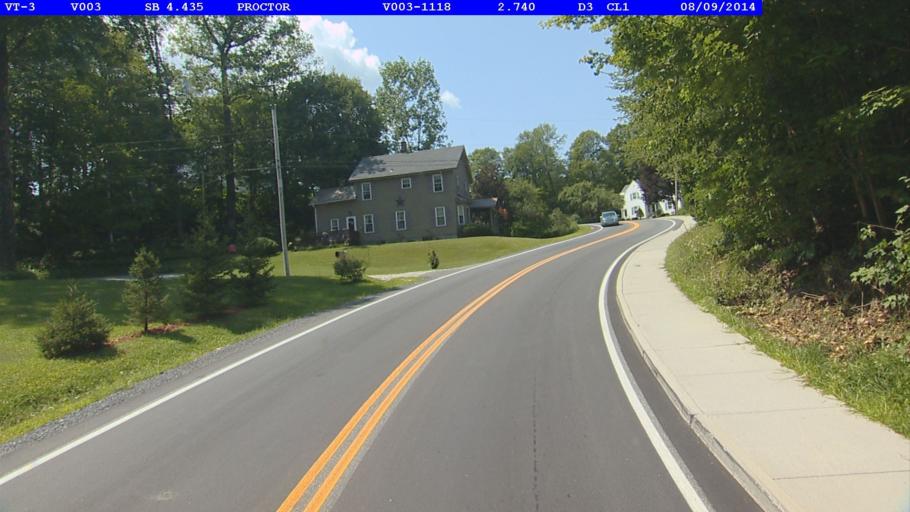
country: US
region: Vermont
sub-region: Rutland County
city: West Rutland
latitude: 43.6621
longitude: -73.0312
